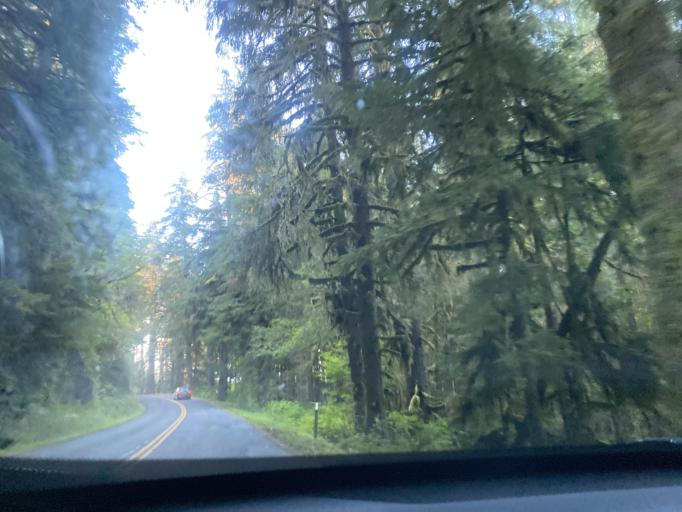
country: US
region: Washington
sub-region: Clallam County
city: Forks
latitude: 47.8109
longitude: -124.1032
